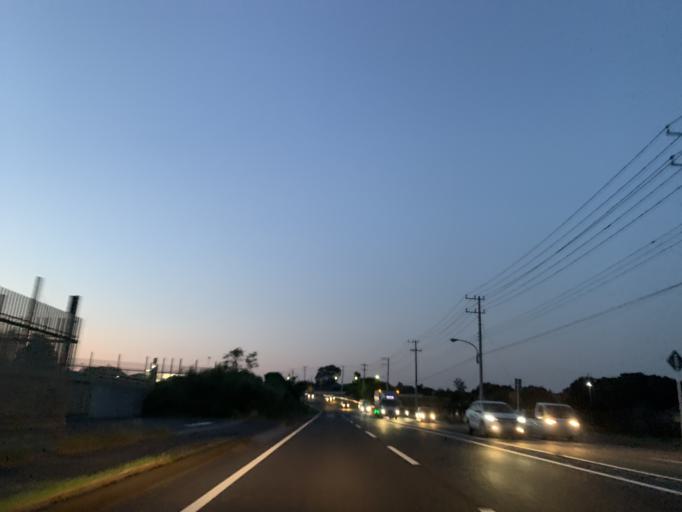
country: JP
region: Chiba
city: Nagareyama
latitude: 35.8741
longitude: 139.9073
